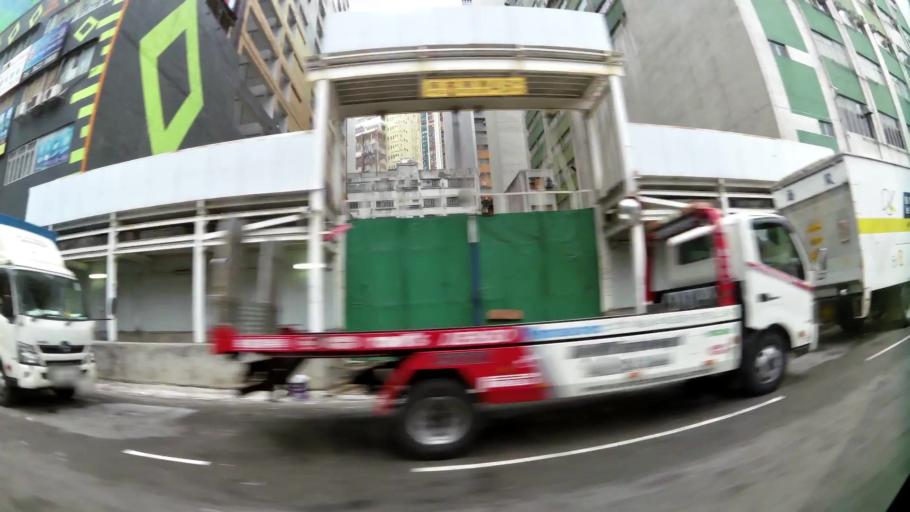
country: HK
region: Tsuen Wan
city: Tsuen Wan
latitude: 22.3642
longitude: 114.1164
